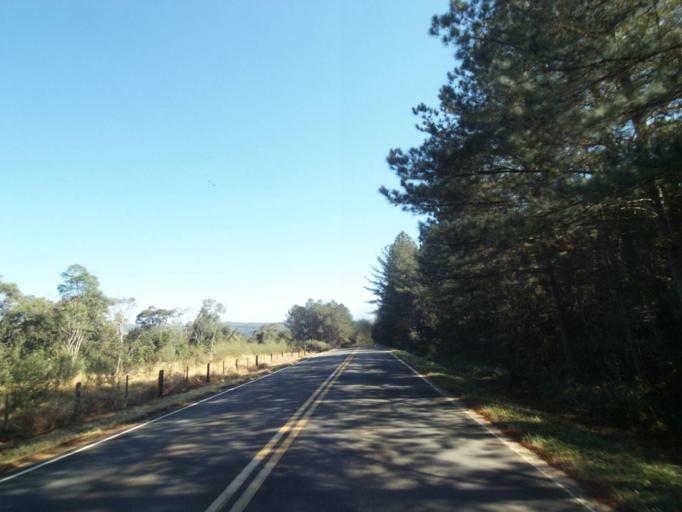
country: BR
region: Parana
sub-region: Tibagi
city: Tibagi
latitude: -24.4791
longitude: -50.4814
